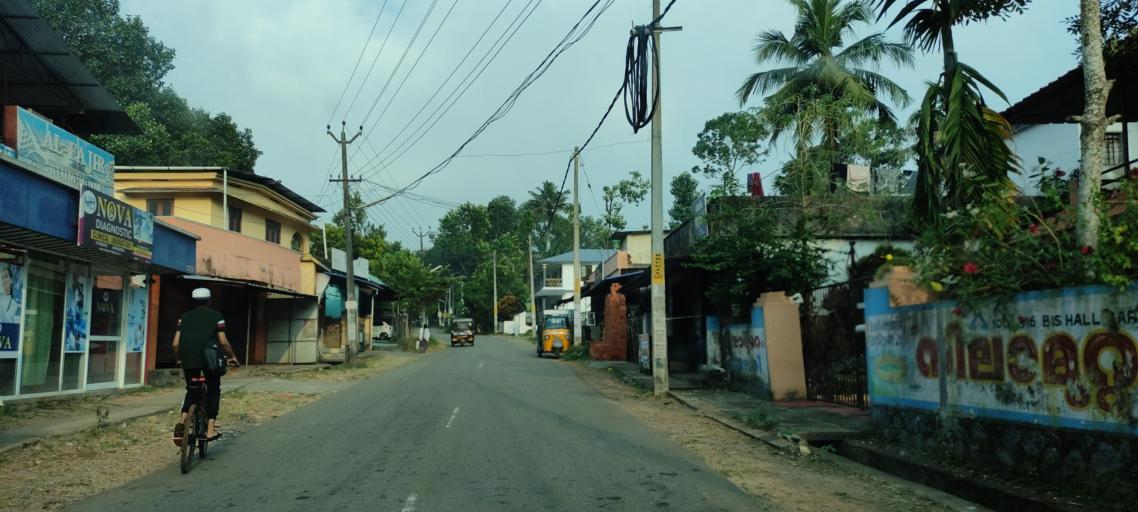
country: IN
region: Kerala
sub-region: Pattanamtitta
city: Adur
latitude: 9.0891
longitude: 76.7446
